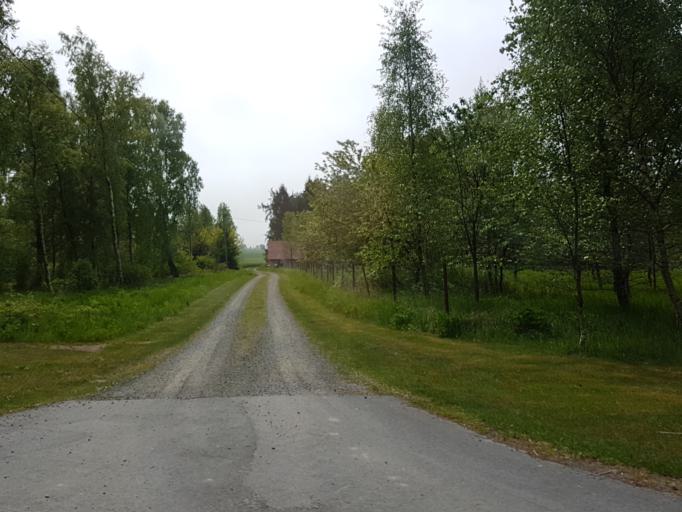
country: SE
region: Skane
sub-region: Tomelilla Kommun
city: Tomelilla
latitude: 55.5132
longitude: 14.0128
